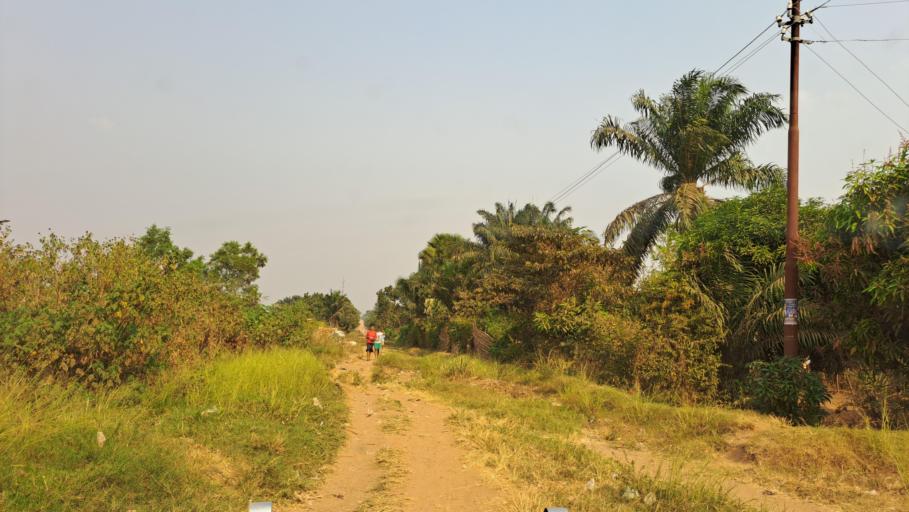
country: CD
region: Kasai-Oriental
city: Mbuji-Mayi
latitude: -6.1347
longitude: 23.5880
